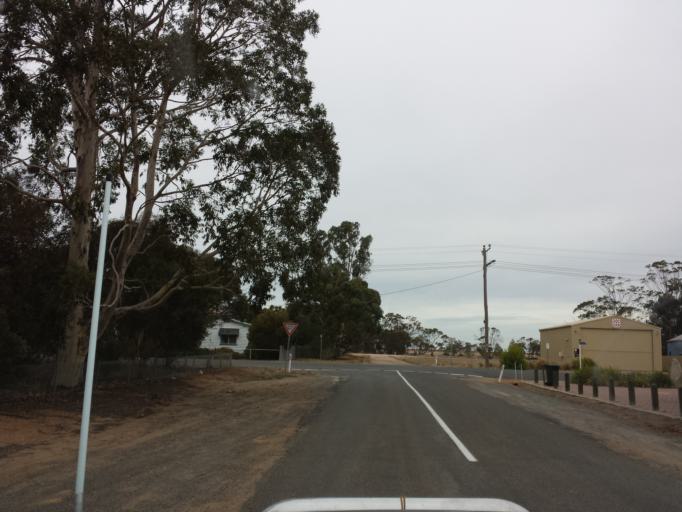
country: AU
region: Victoria
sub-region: Horsham
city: Horsham
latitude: -36.0757
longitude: 142.4167
